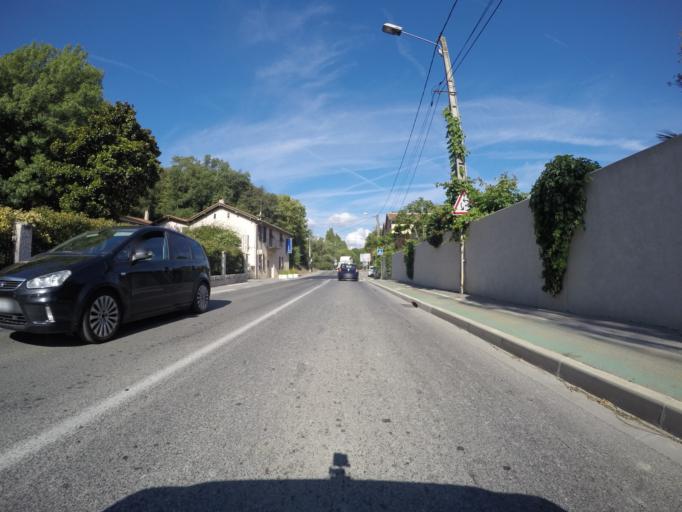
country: FR
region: Provence-Alpes-Cote d'Azur
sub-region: Departement des Alpes-Maritimes
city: Villeneuve-Loubet
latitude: 43.6560
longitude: 7.1226
